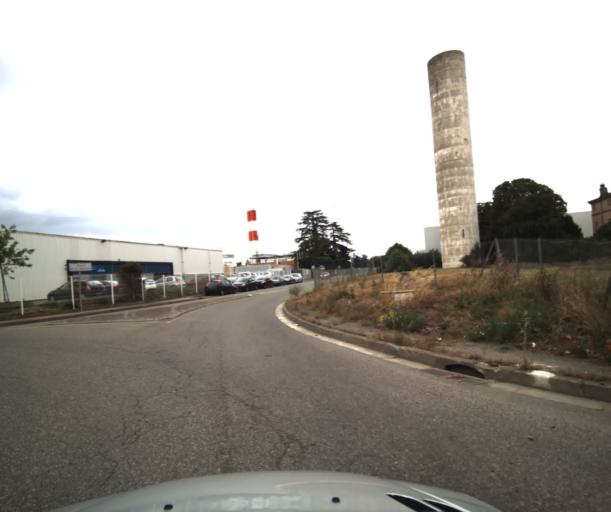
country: FR
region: Midi-Pyrenees
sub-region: Departement de la Haute-Garonne
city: Pinsaguel
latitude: 43.5293
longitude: 1.3801
